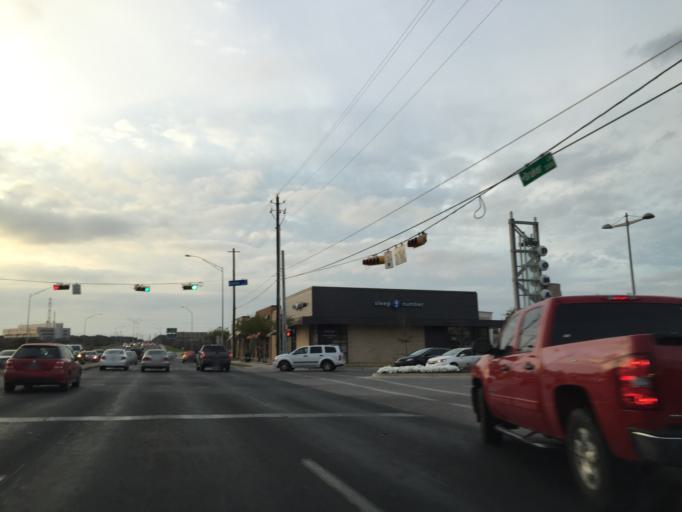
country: US
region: Texas
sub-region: Travis County
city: Wells Branch
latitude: 30.3922
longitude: -97.7253
